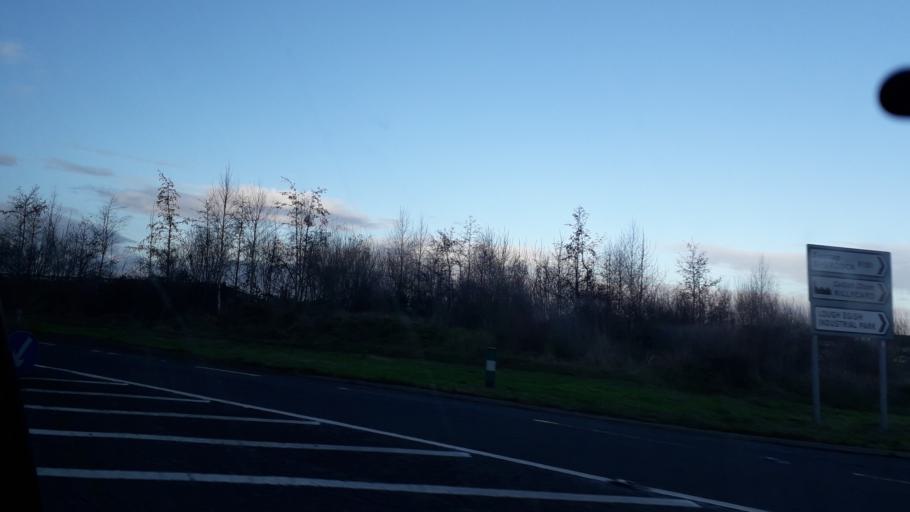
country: IE
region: Ulster
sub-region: County Monaghan
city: Castleblayney
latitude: 54.1154
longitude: -6.7571
